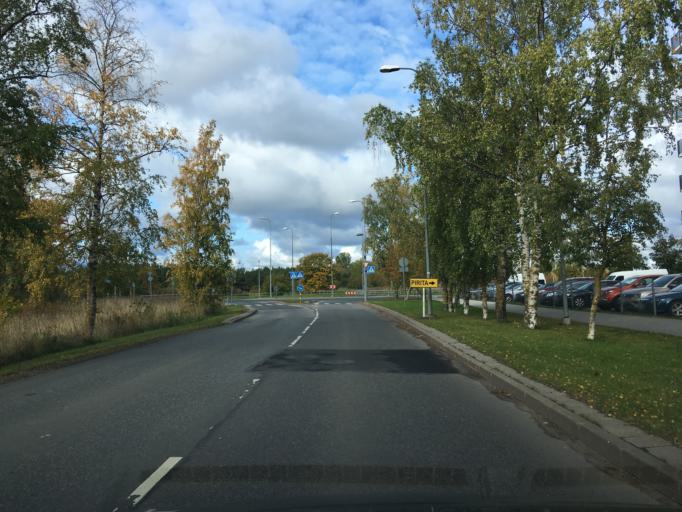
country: EE
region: Harju
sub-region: Viimsi vald
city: Viimsi
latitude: 59.4469
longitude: 24.8247
